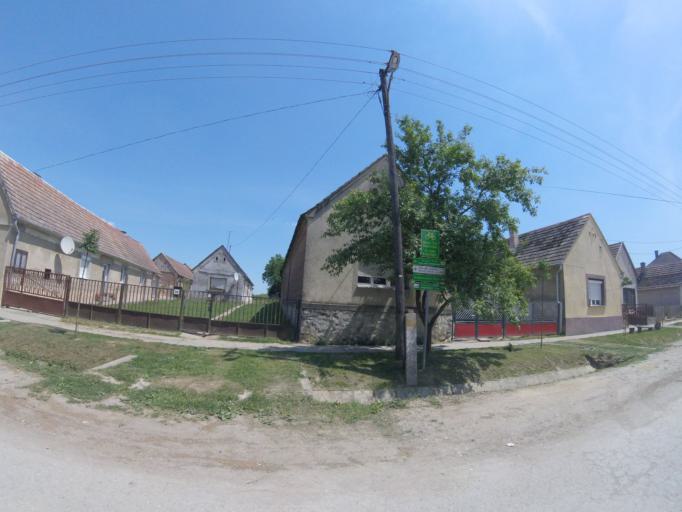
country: HU
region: Baranya
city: Sellye
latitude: 45.8232
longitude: 17.8220
